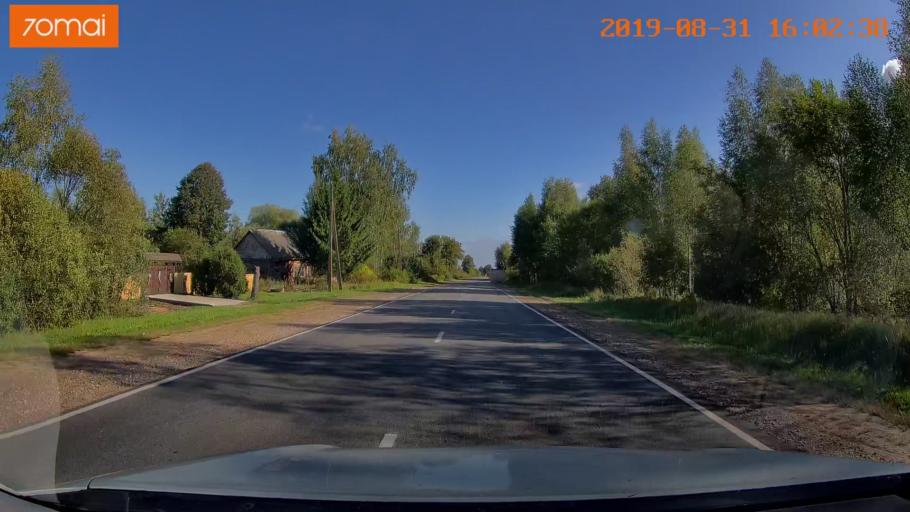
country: RU
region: Kaluga
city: Yukhnov
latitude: 54.6729
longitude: 35.3051
